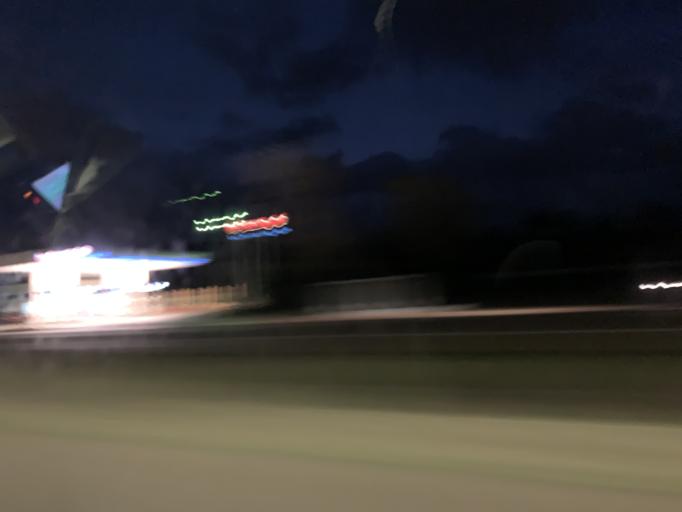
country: ES
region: Extremadura
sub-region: Provincia de Badajoz
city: Badajoz
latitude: 38.8880
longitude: -6.9220
